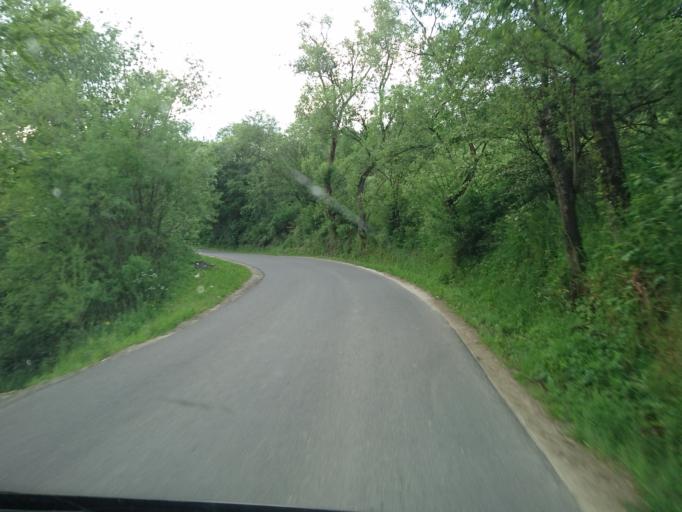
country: PL
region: Lesser Poland Voivodeship
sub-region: Powiat nowotarski
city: Lopuszna
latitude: 49.4831
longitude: 20.1845
